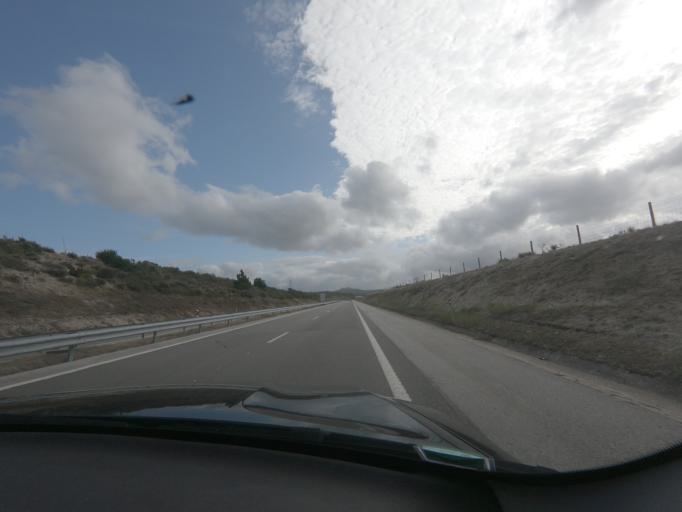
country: PT
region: Viseu
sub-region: Tarouca
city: Tarouca
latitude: 41.0278
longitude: -7.8703
